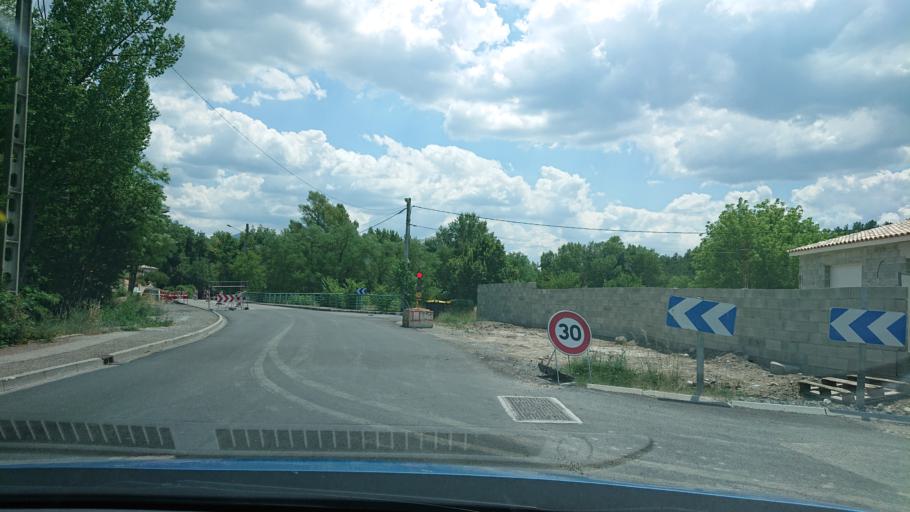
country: FR
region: Provence-Alpes-Cote d'Azur
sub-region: Departement des Alpes-de-Haute-Provence
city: Mallemoisson
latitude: 44.0759
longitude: 6.1758
